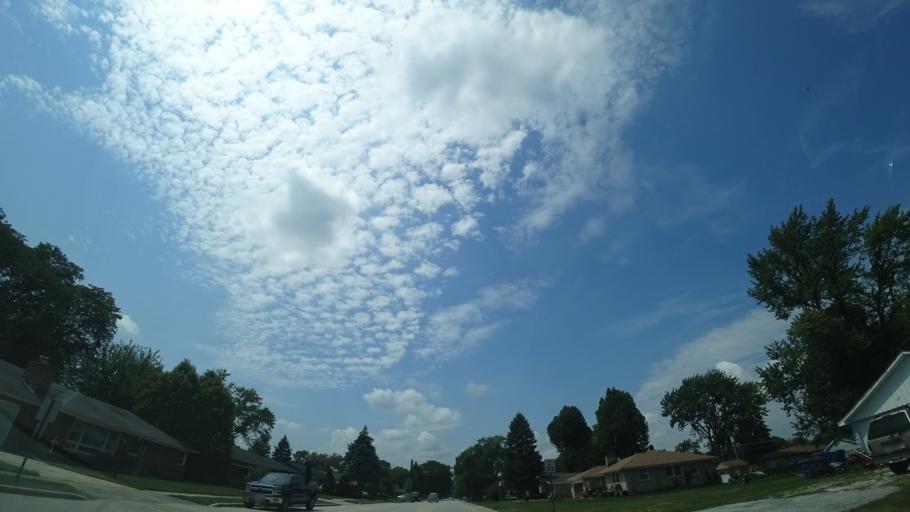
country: US
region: Illinois
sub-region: Cook County
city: Worth
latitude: 41.6828
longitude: -87.7885
